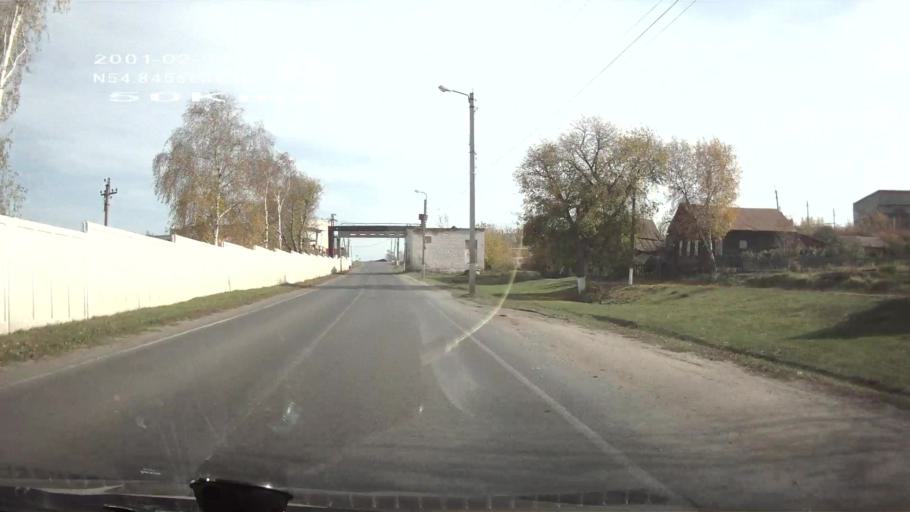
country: RU
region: Mordoviya
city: Turgenevo
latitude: 54.8459
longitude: 46.3395
